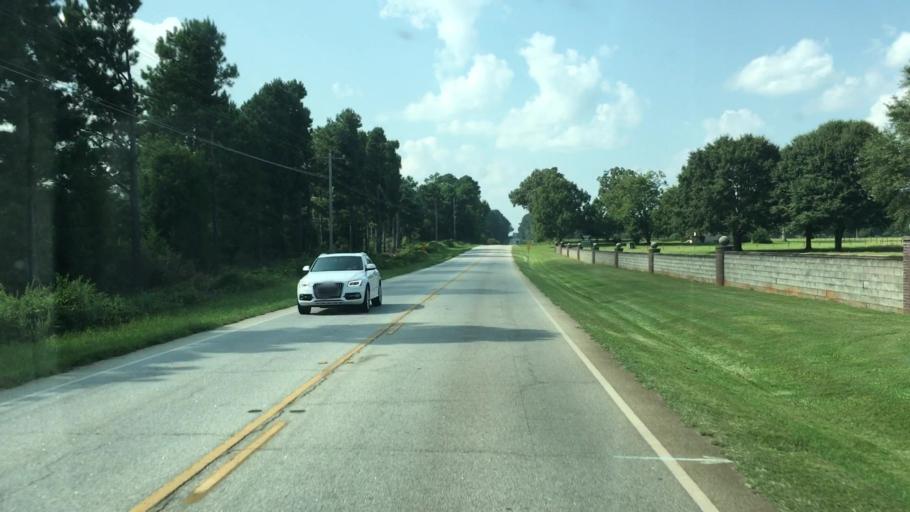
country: US
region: Georgia
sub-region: Walton County
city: Social Circle
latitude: 33.5683
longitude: -83.7392
